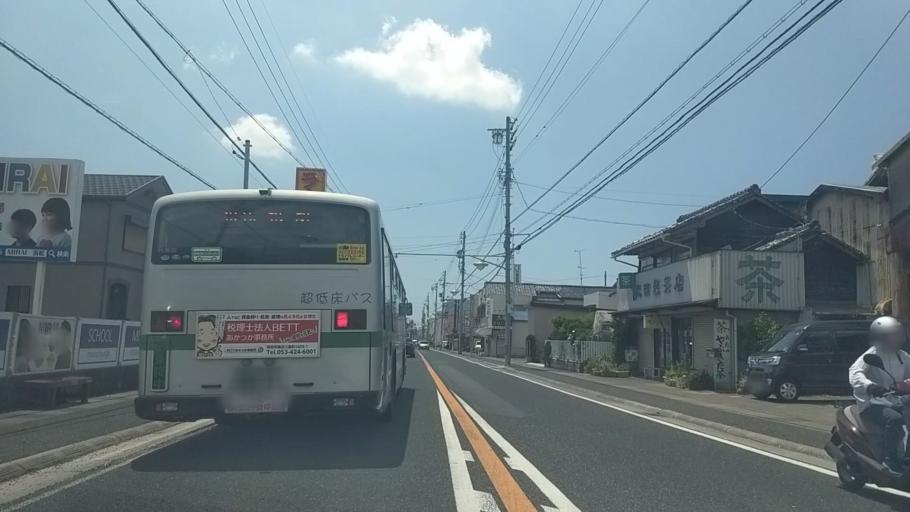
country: JP
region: Shizuoka
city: Hamamatsu
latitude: 34.7390
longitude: 137.7237
